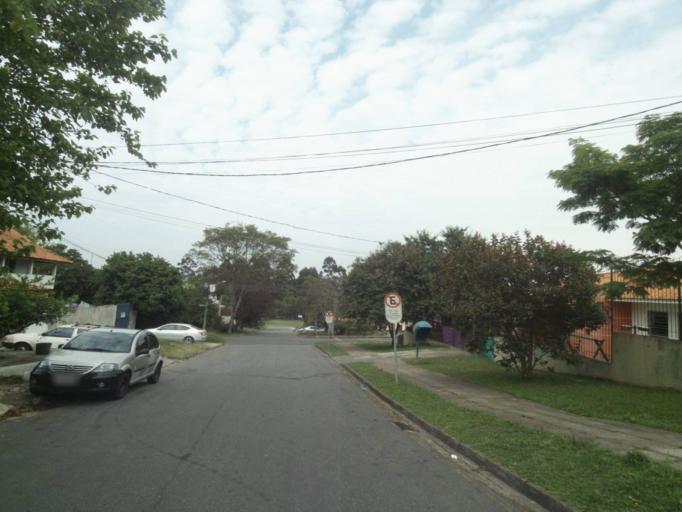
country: BR
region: Parana
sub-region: Pinhais
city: Pinhais
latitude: -25.4225
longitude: -49.2076
